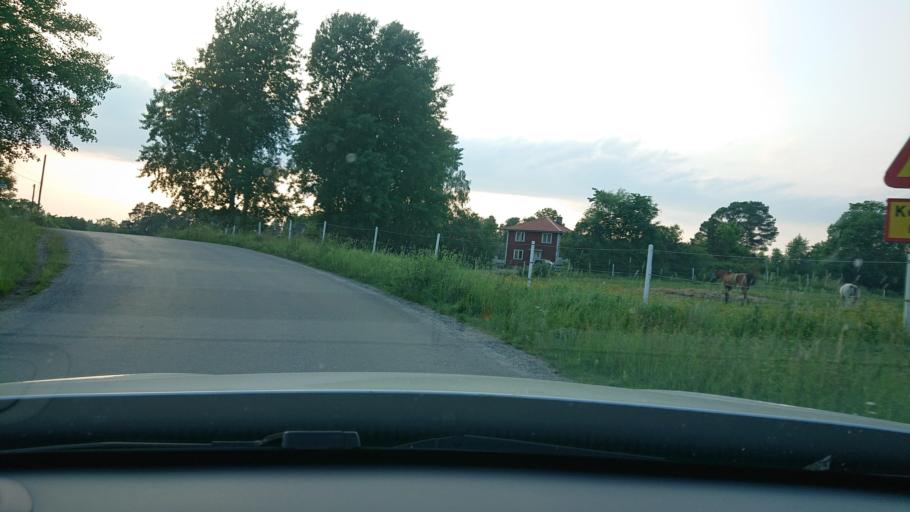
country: SE
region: Stockholm
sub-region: Osterakers Kommun
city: Akersberga
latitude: 59.5061
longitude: 18.3241
